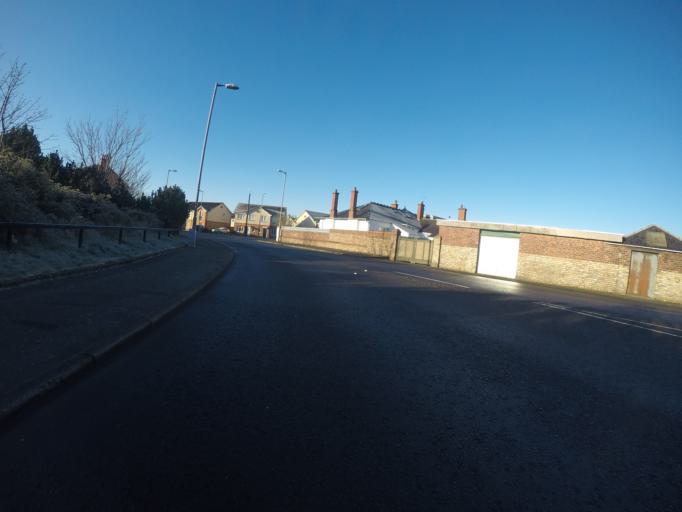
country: GB
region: Scotland
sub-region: North Ayrshire
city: Stevenston
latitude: 55.6338
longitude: -4.7438
